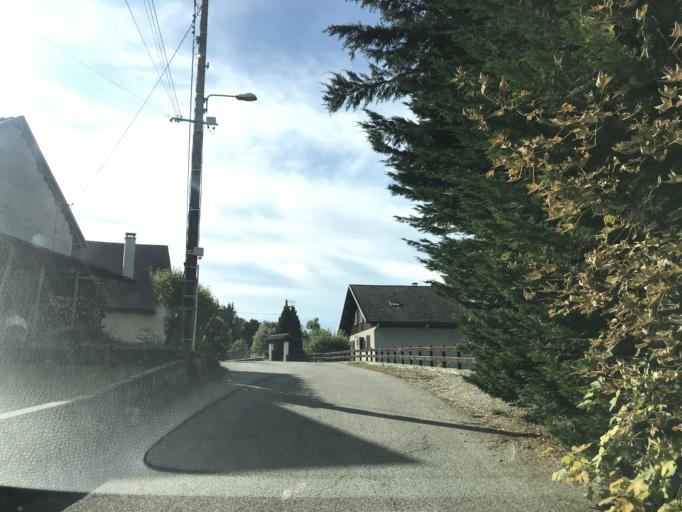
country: FR
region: Rhone-Alpes
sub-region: Departement de la Savoie
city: Novalaise
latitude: 45.6321
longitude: 5.8004
